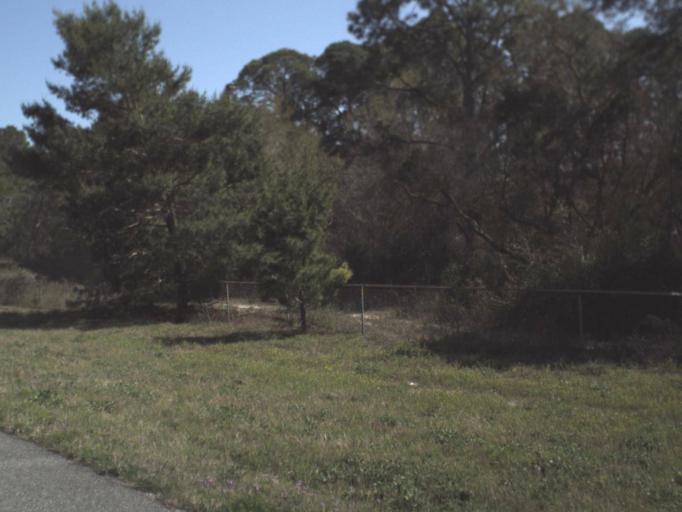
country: US
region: Florida
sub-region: Franklin County
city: Carrabelle
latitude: 29.9324
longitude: -84.4404
